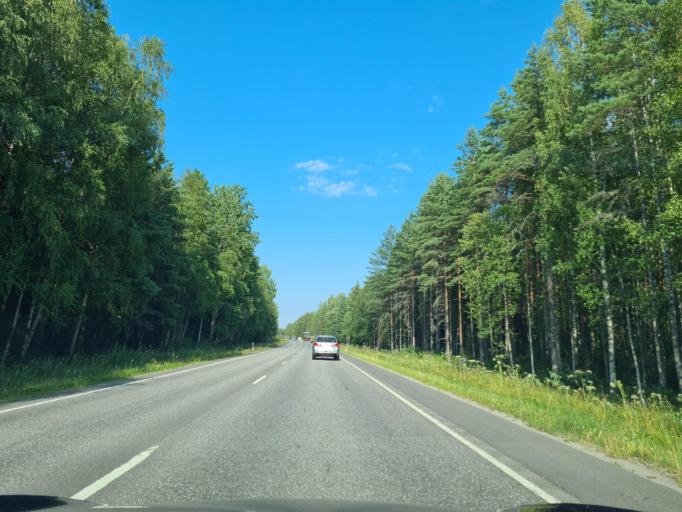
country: FI
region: Satakunta
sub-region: Pohjois-Satakunta
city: Kankaanpaeae
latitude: 61.8383
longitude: 22.4396
